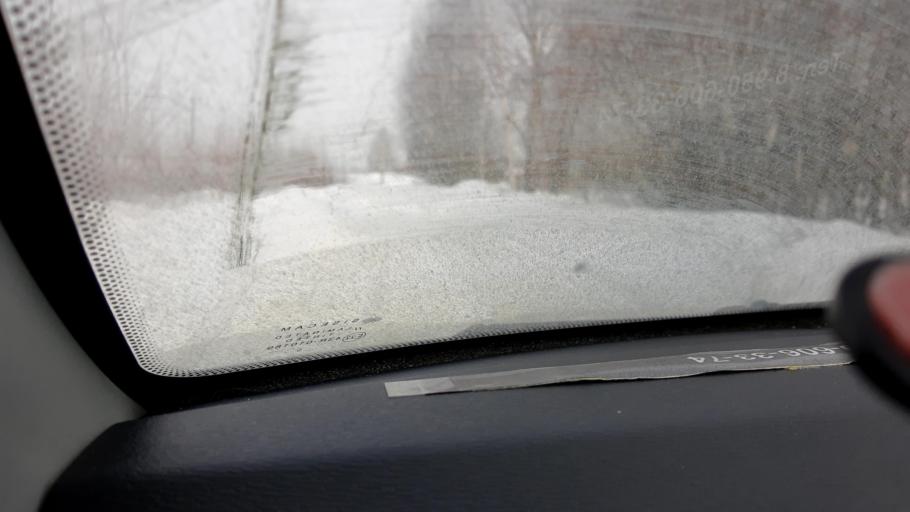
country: RU
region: Nizjnij Novgorod
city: Sitniki
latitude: 56.5253
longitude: 44.0530
